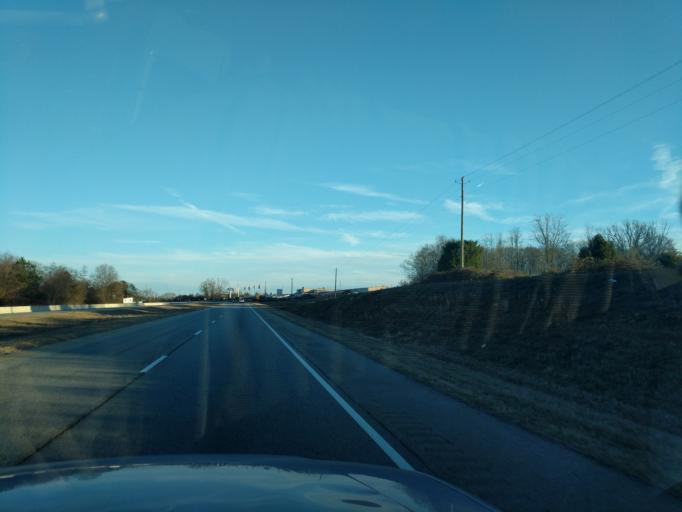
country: US
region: Georgia
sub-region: Franklin County
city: Lavonia
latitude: 34.4503
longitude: -83.1464
